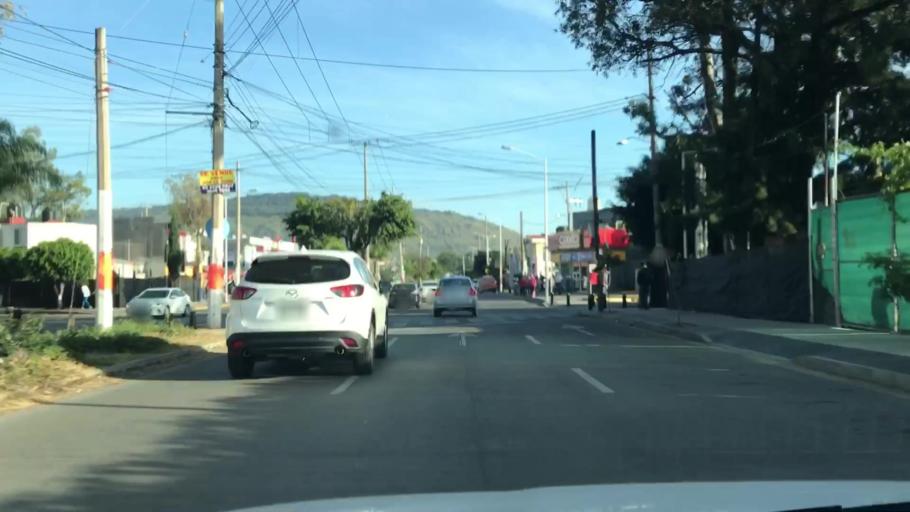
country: MX
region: Jalisco
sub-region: Tlajomulco de Zuniga
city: Palomar
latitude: 20.6275
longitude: -103.4607
